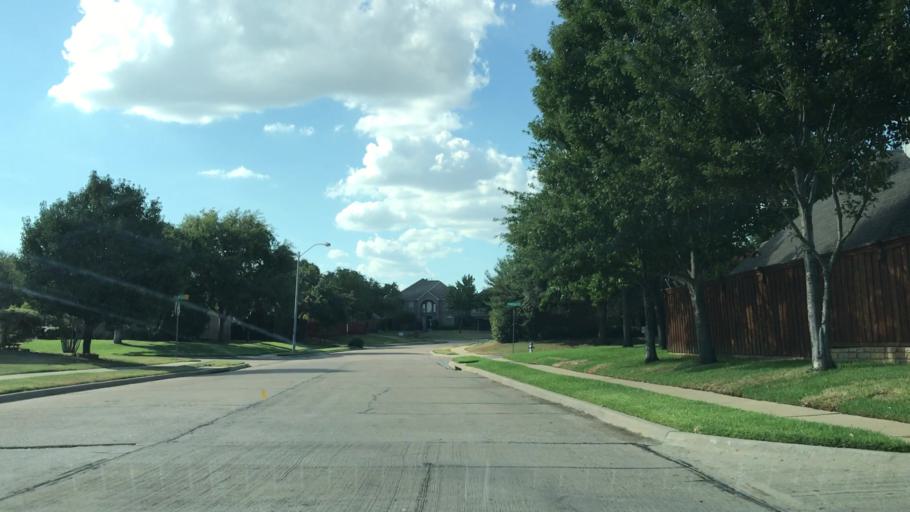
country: US
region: Texas
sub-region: Dallas County
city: Coppell
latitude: 32.9396
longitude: -96.9619
